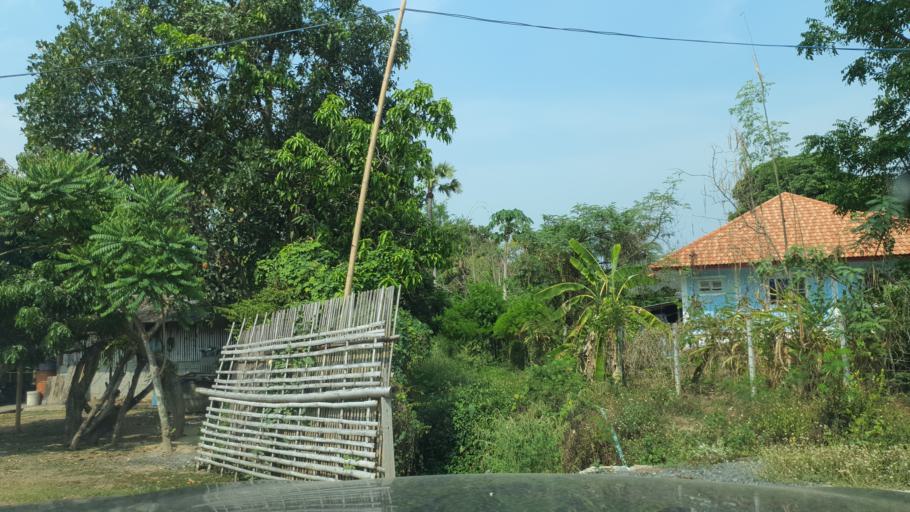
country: TH
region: Chiang Mai
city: Mae On
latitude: 18.7354
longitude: 99.2007
